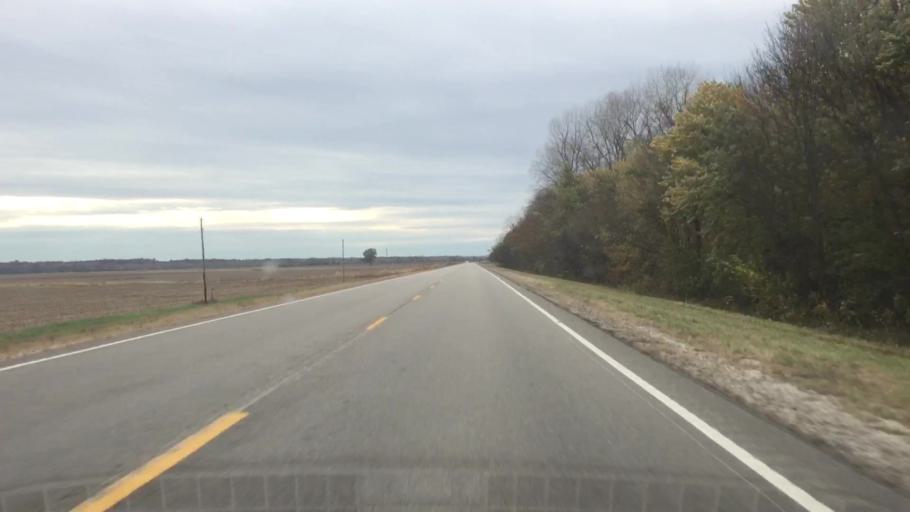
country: US
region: Missouri
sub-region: Callaway County
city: Holts Summit
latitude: 38.5817
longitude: -92.0708
